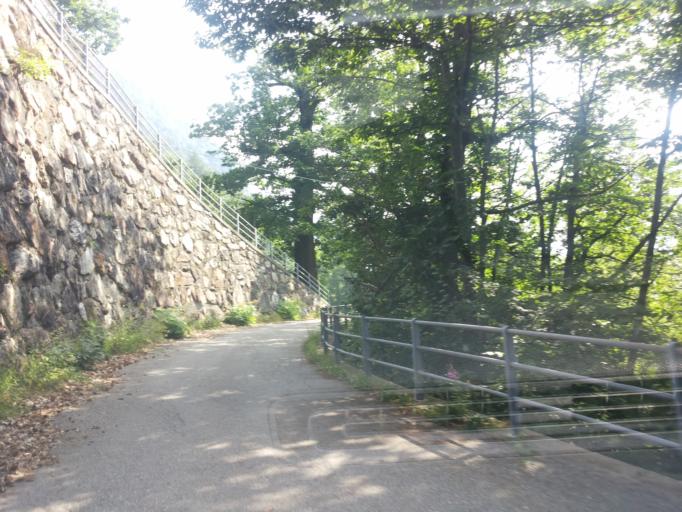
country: IT
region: Aosta Valley
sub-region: Valle d'Aosta
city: Fontainemore
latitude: 45.6431
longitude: 7.8612
